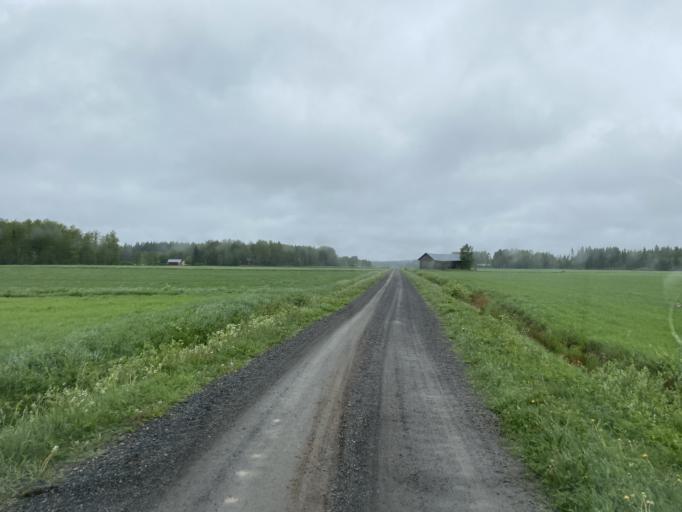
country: FI
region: Pirkanmaa
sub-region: Etelae-Pirkanmaa
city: Urjala
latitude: 60.9615
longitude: 23.5917
